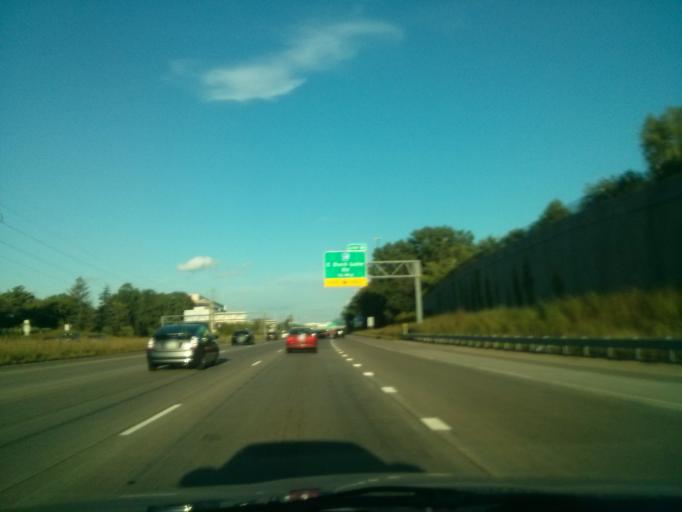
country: US
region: Minnesota
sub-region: Hennepin County
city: Edina
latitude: 44.8601
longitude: -93.3742
